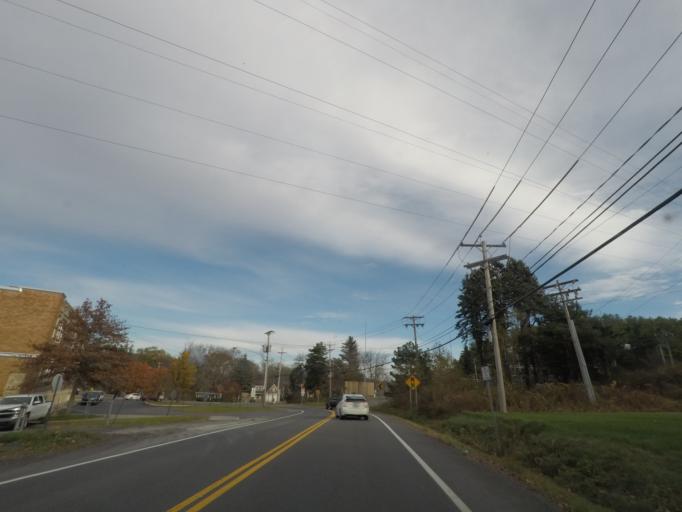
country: US
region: New York
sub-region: Albany County
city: Voorheesville
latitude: 42.6481
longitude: -73.9367
